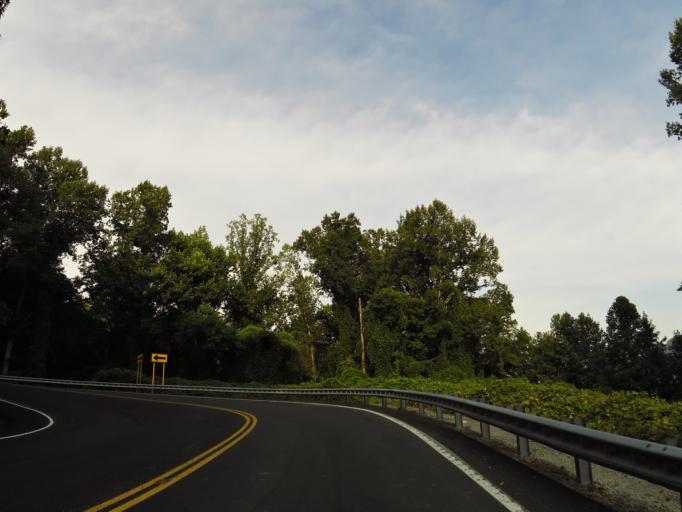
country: US
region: Tennessee
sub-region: Morgan County
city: Coalfield
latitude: 36.1043
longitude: -84.4456
